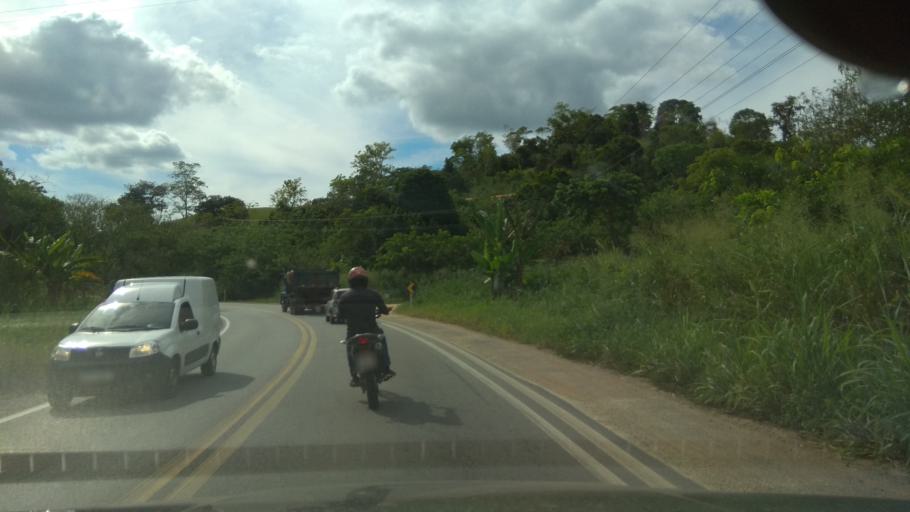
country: BR
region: Bahia
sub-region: Ipiau
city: Ipiau
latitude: -14.0980
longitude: -39.7774
